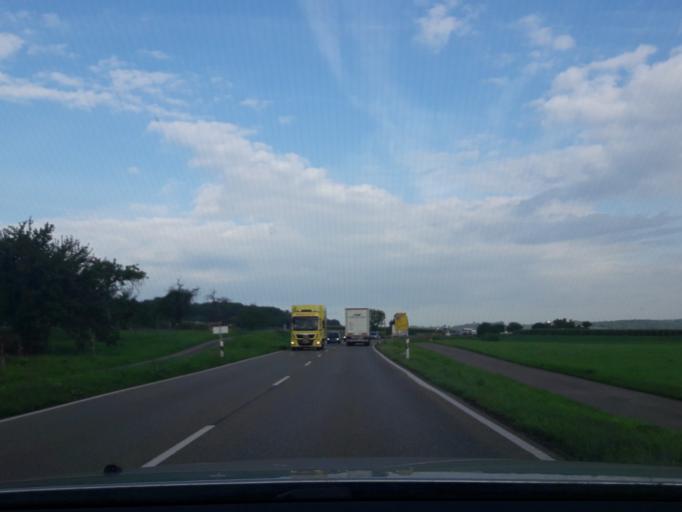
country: DE
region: Baden-Wuerttemberg
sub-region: Regierungsbezirk Stuttgart
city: Aspach
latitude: 48.9781
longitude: 9.3734
